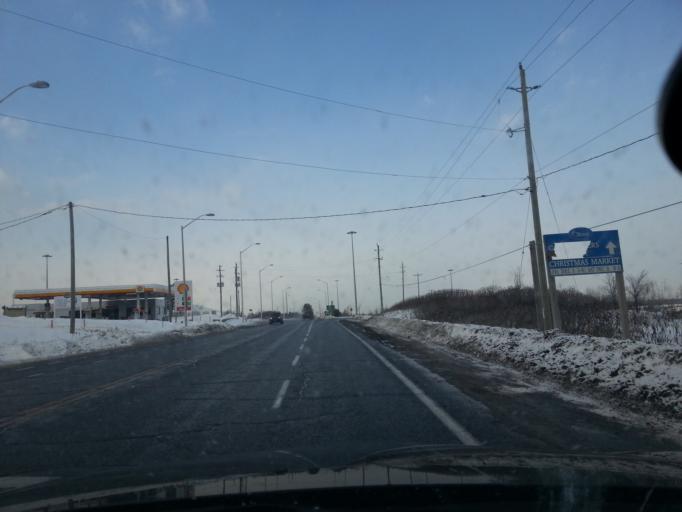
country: CA
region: Ontario
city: Bells Corners
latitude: 45.2787
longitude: -75.9539
